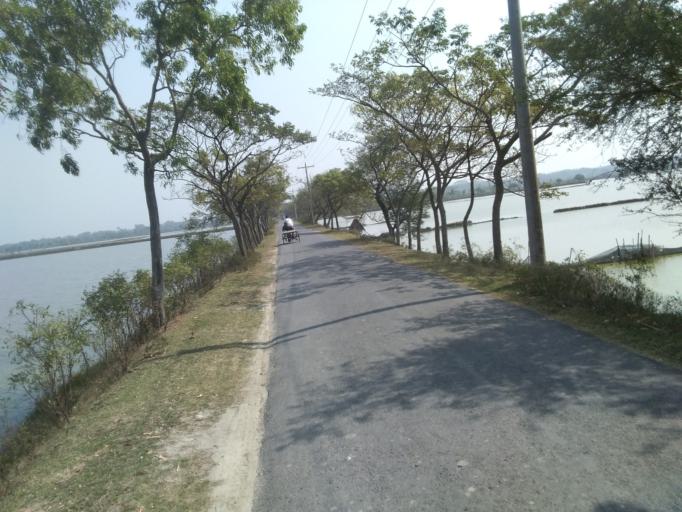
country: IN
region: West Bengal
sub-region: North 24 Parganas
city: Taki
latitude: 22.5938
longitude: 88.9837
